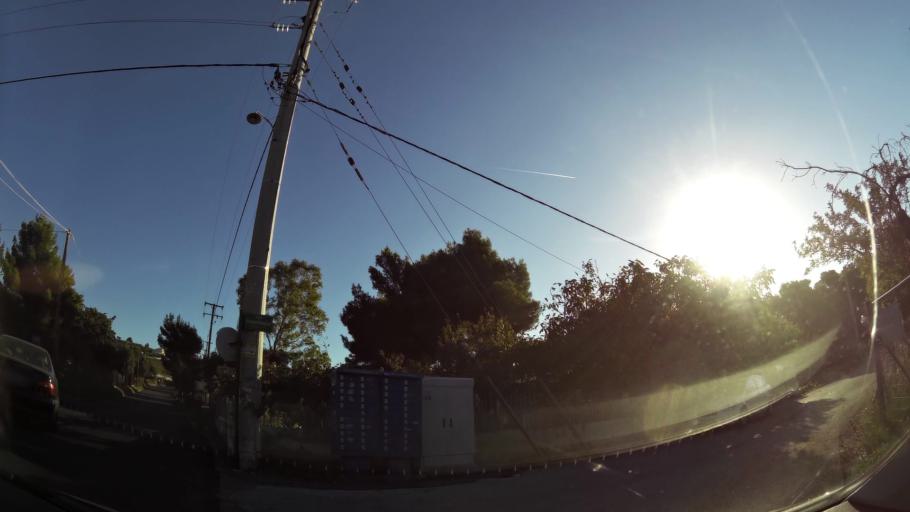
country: GR
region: Attica
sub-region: Nomarchia Anatolikis Attikis
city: Pallini
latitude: 38.0102
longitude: 23.8914
